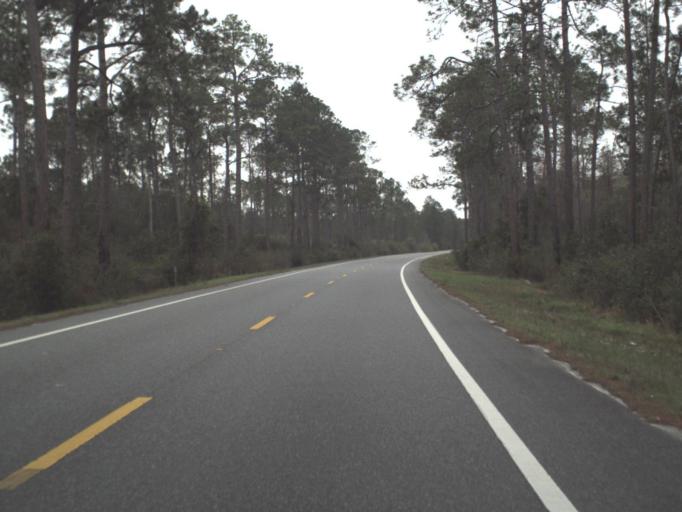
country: US
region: Florida
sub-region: Franklin County
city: Apalachicola
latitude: 29.9758
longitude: -84.9750
